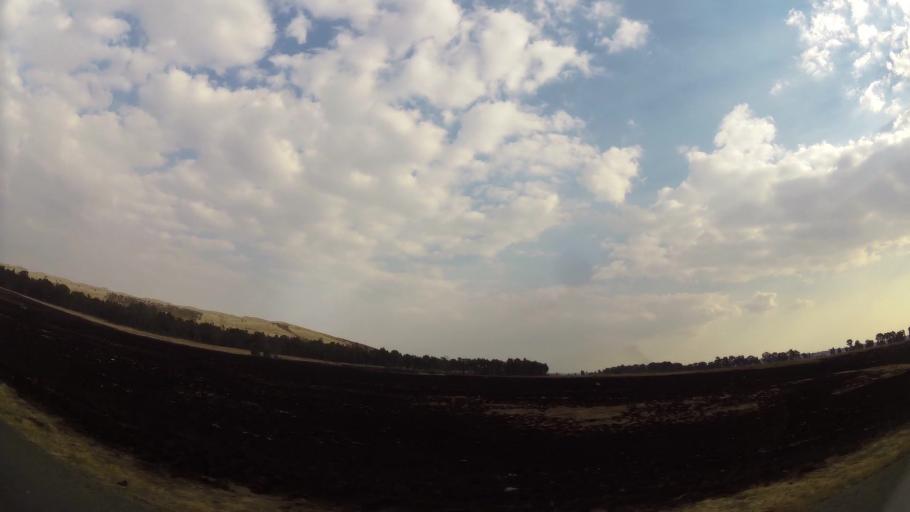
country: ZA
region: Gauteng
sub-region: Ekurhuleni Metropolitan Municipality
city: Springs
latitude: -26.2836
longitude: 28.5298
